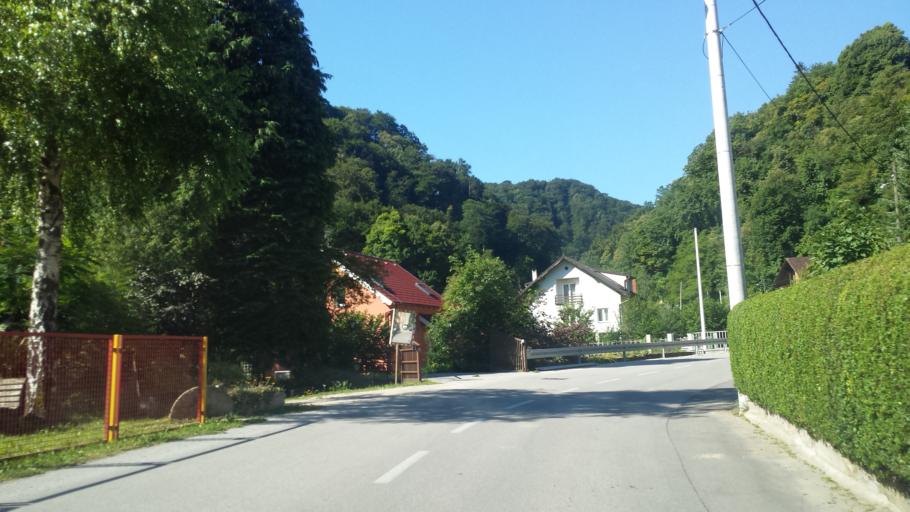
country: HR
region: Zagrebacka
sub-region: Grad Samobor
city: Samobor
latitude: 45.7984
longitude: 15.6950
